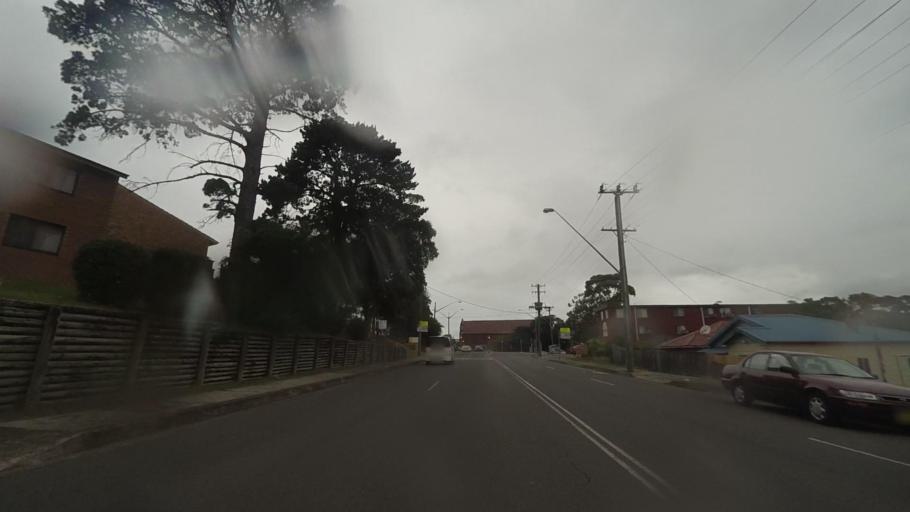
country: AU
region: New South Wales
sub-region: Wollongong
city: West Wollongong
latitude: -34.4249
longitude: 150.8702
